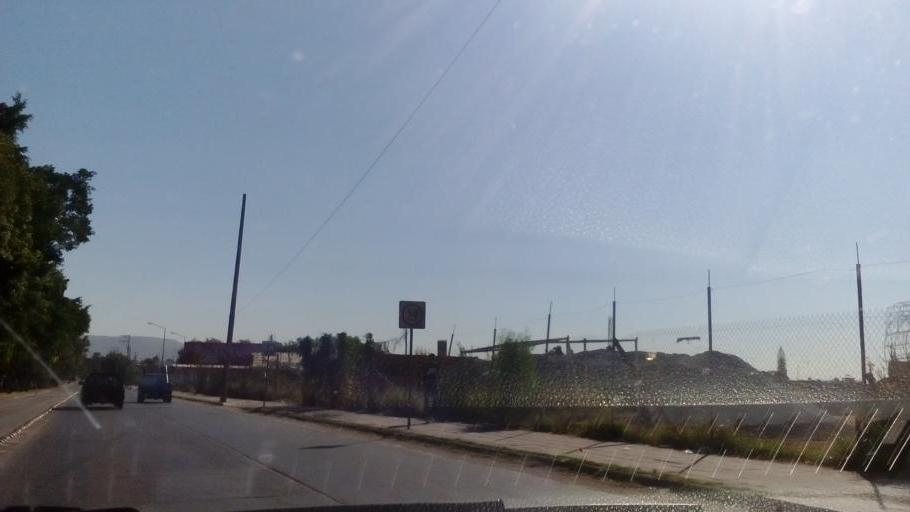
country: MX
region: Guanajuato
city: Leon
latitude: 21.1475
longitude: -101.6806
